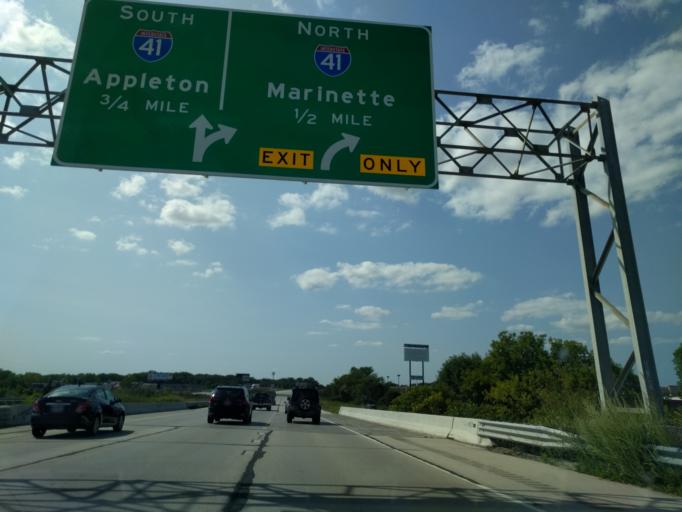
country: US
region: Wisconsin
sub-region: Brown County
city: Ashwaubenon
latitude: 44.4790
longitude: -88.0632
